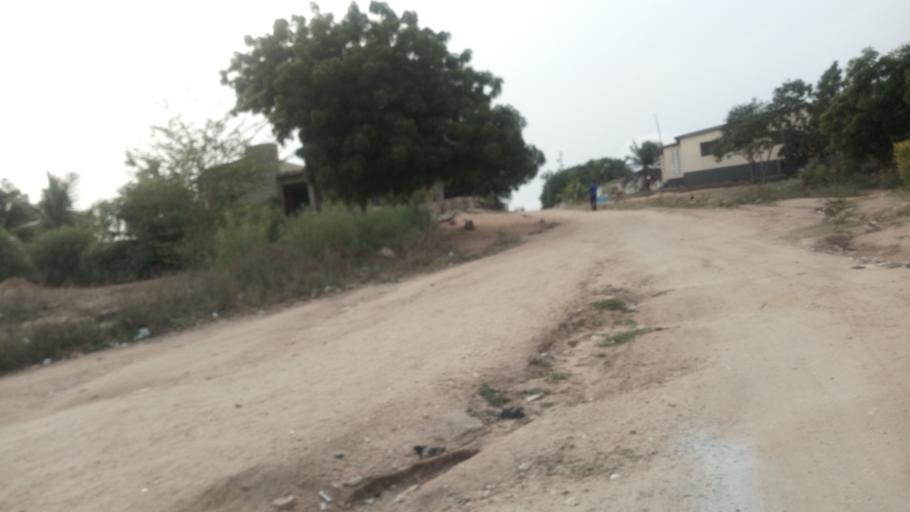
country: GH
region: Central
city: Winneba
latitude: 5.3563
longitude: -0.6229
